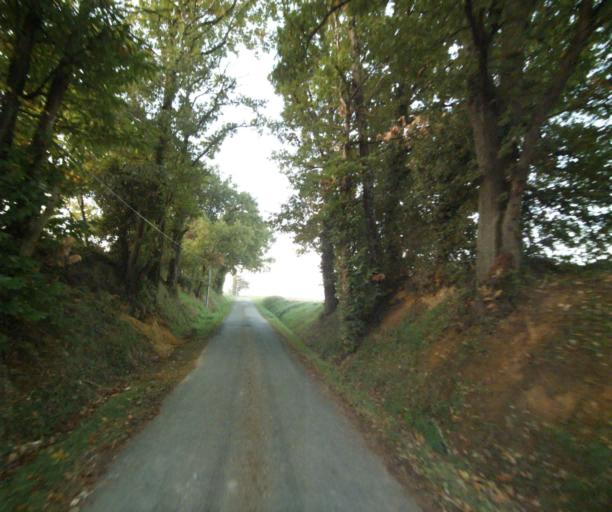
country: FR
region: Midi-Pyrenees
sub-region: Departement du Gers
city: Gondrin
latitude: 43.7946
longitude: 0.2128
